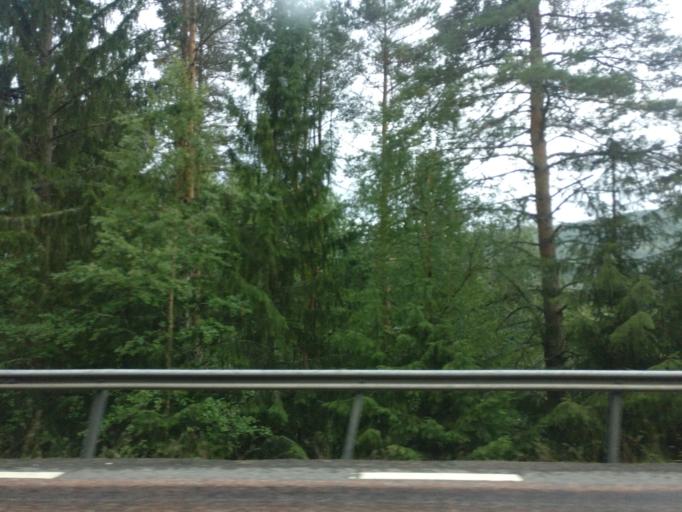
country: SE
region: Vaermland
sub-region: Torsby Kommun
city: Torsby
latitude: 60.7012
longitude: 12.9083
